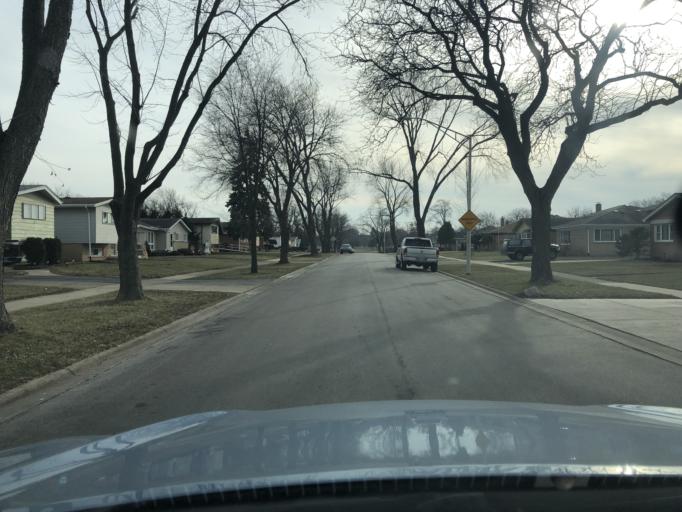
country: US
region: Illinois
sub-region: DuPage County
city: Addison
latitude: 41.9291
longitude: -87.9936
